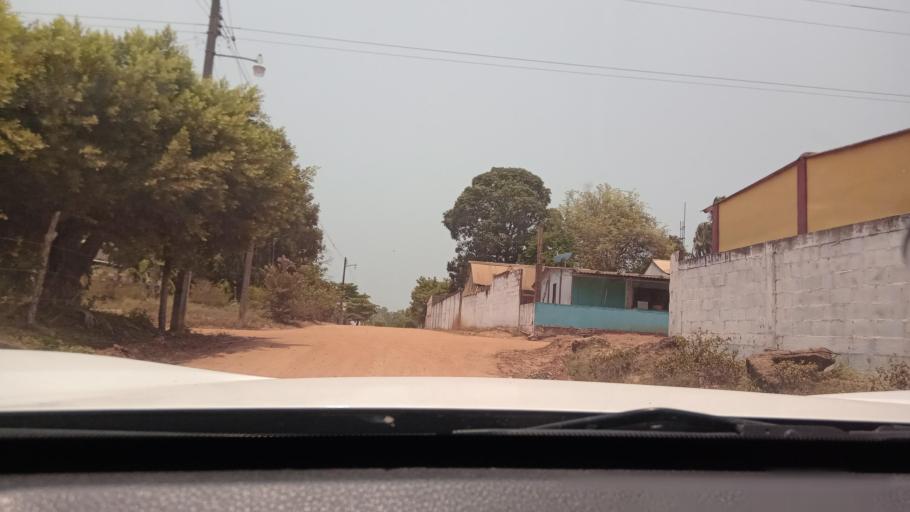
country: MX
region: Veracruz
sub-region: Acayucan
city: Ixhuapan
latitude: 18.0193
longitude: -94.7822
